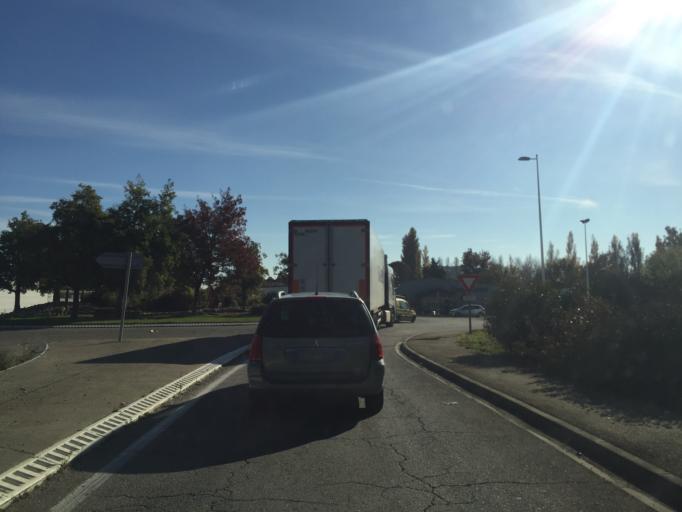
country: FR
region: Provence-Alpes-Cote d'Azur
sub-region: Departement du Vaucluse
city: Vedene
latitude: 43.9902
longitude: 4.8917
